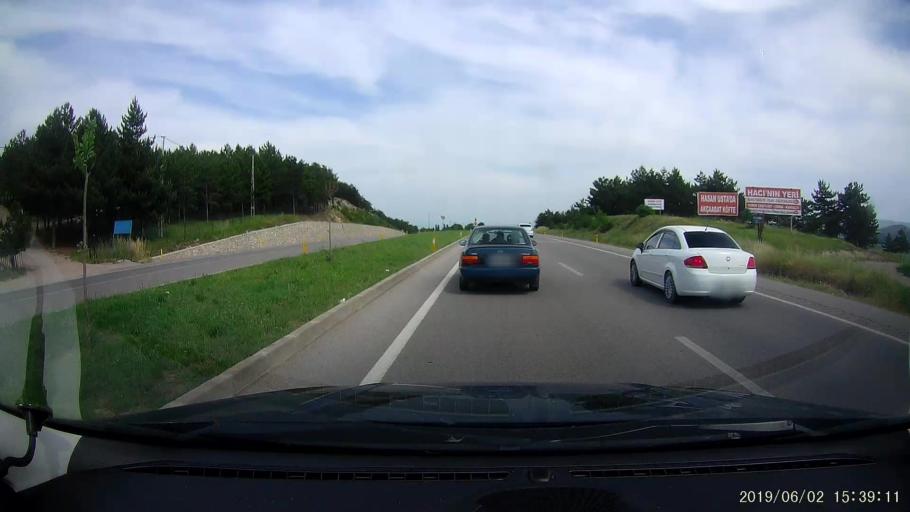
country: TR
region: Amasya
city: Gumushacikoy
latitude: 40.8682
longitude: 35.2553
